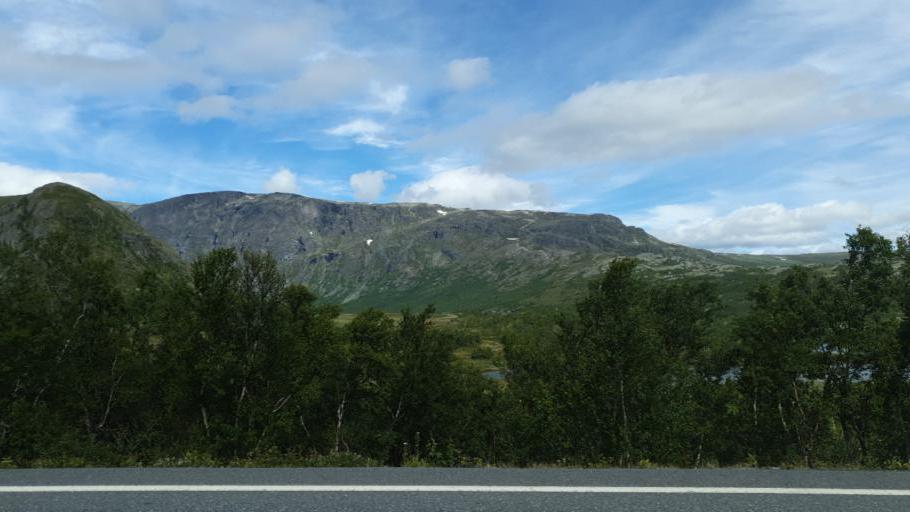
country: NO
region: Oppland
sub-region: Oystre Slidre
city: Heggenes
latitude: 61.4783
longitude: 8.8264
